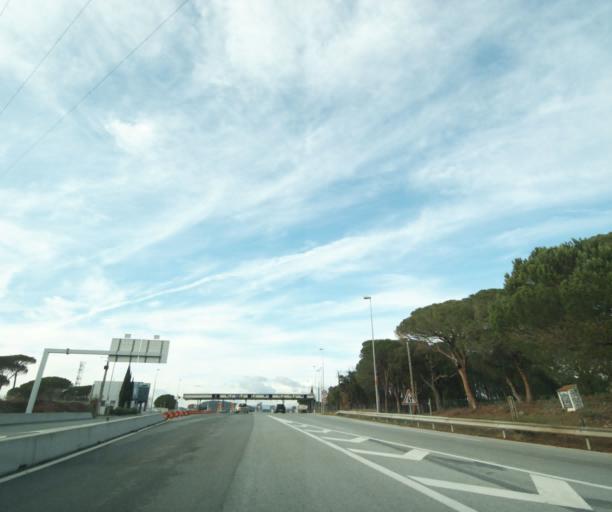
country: FR
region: Provence-Alpes-Cote d'Azur
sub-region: Departement du Var
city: Le Muy
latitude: 43.4599
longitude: 6.5524
